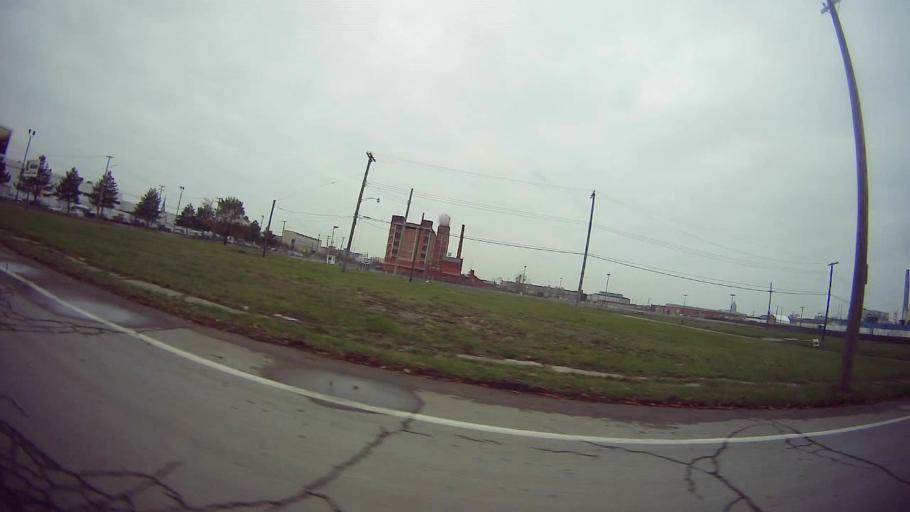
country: US
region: Michigan
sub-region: Wayne County
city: Hamtramck
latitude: 42.3648
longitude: -83.0446
